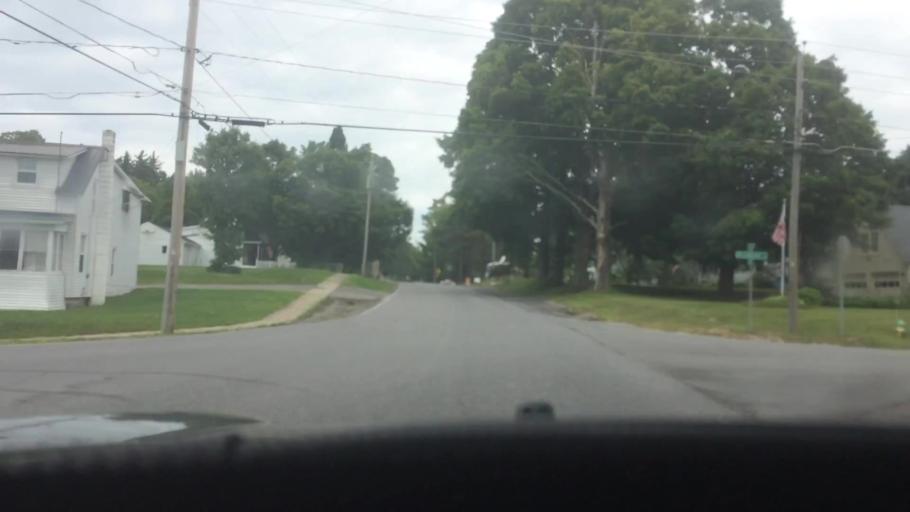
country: US
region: New York
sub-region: St. Lawrence County
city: Hannawa Falls
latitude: 44.5539
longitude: -74.9299
